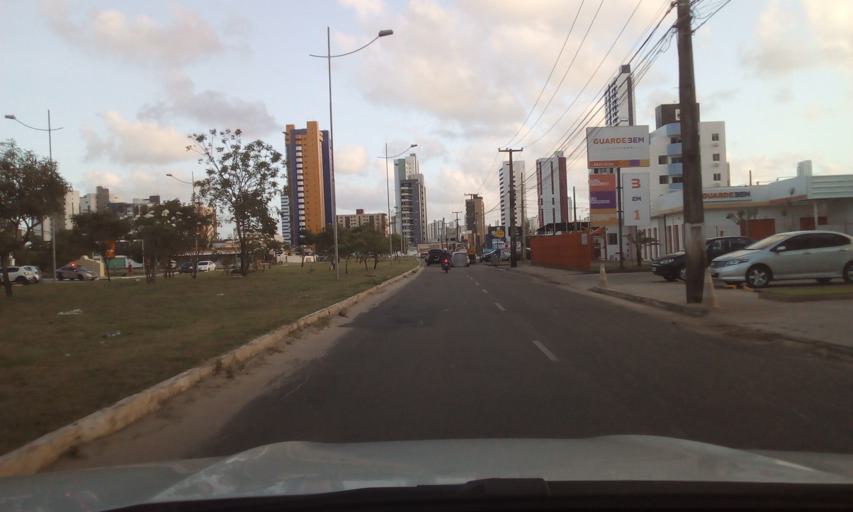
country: BR
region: Paraiba
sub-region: Joao Pessoa
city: Joao Pessoa
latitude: -7.0853
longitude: -34.8400
